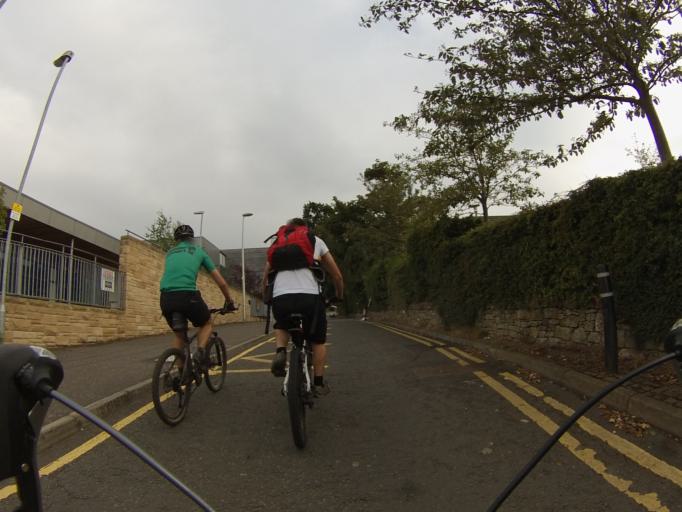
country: GB
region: Scotland
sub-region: Edinburgh
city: Colinton
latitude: 55.9000
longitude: -3.2595
